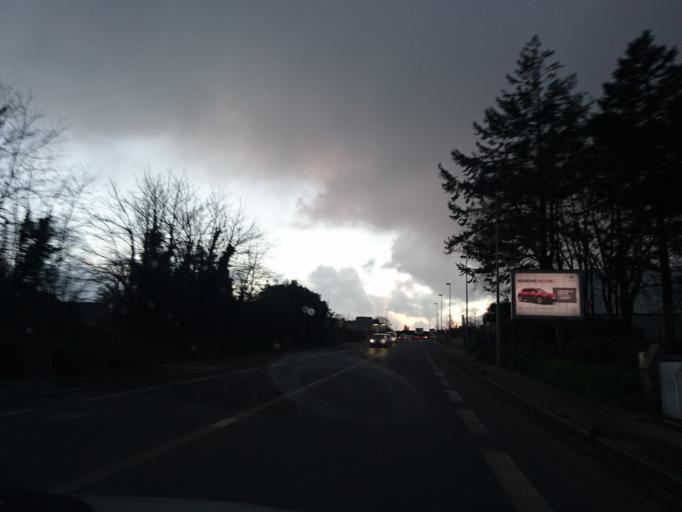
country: FR
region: Brittany
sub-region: Departement du Finistere
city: Guipavas
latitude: 48.4164
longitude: -4.4332
